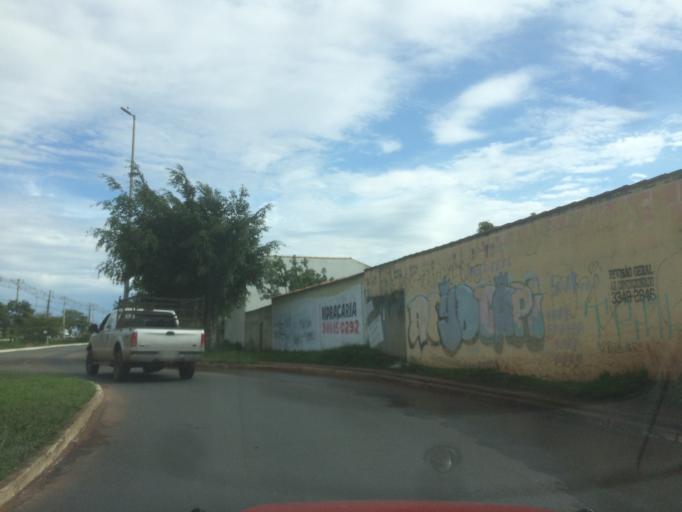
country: BR
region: Federal District
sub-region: Brasilia
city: Brasilia
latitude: -15.8752
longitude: -47.8227
